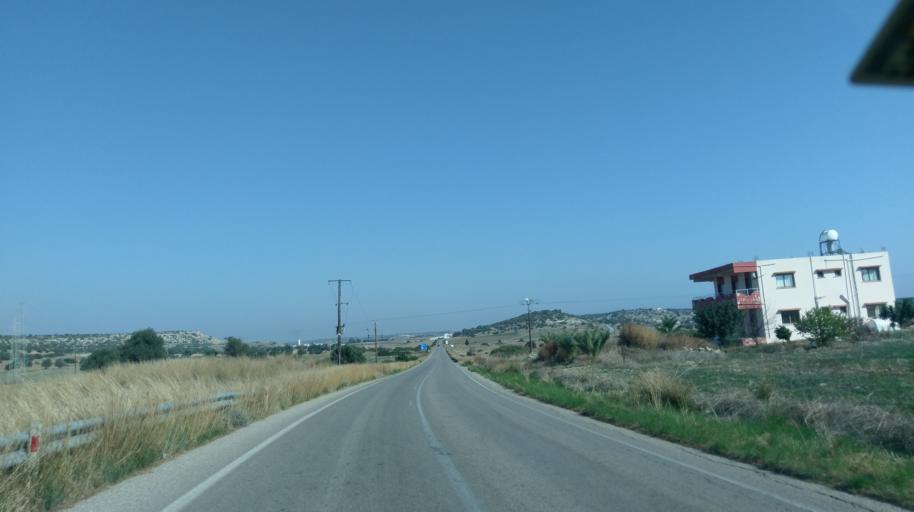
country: CY
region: Ammochostos
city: Leonarisso
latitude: 35.3946
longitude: 34.0618
